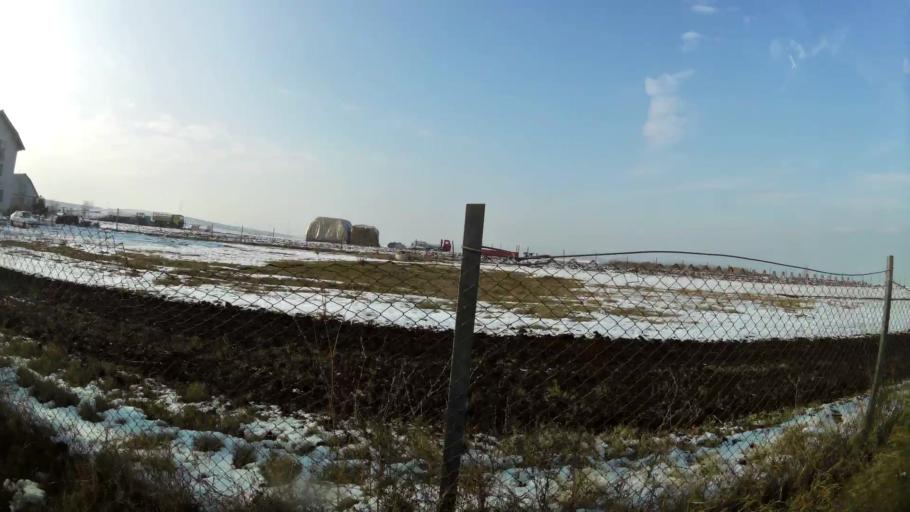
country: MK
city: Creshevo
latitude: 42.0223
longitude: 21.4980
